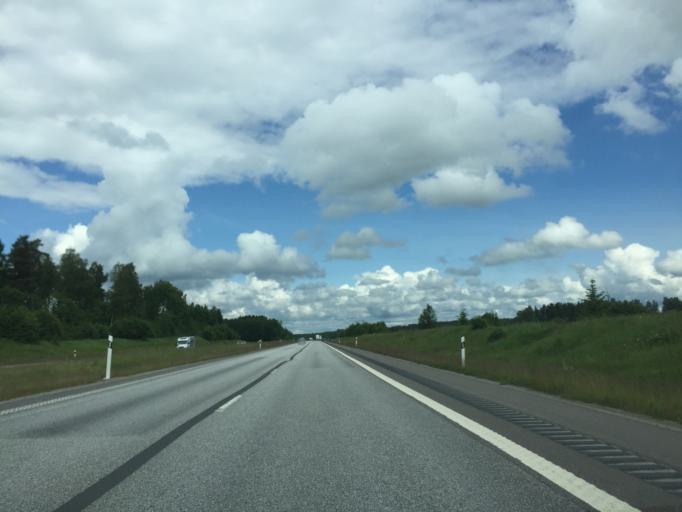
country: SE
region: Vaestmanland
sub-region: Arboga Kommun
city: Arboga
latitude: 59.4468
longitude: 15.8996
